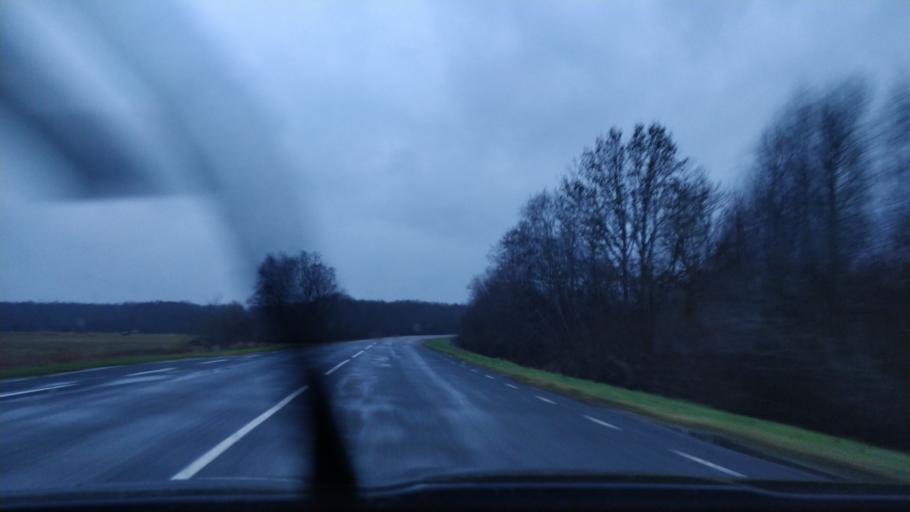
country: EE
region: Laeaene
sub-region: Lihula vald
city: Lihula
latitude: 58.7048
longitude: 23.8619
